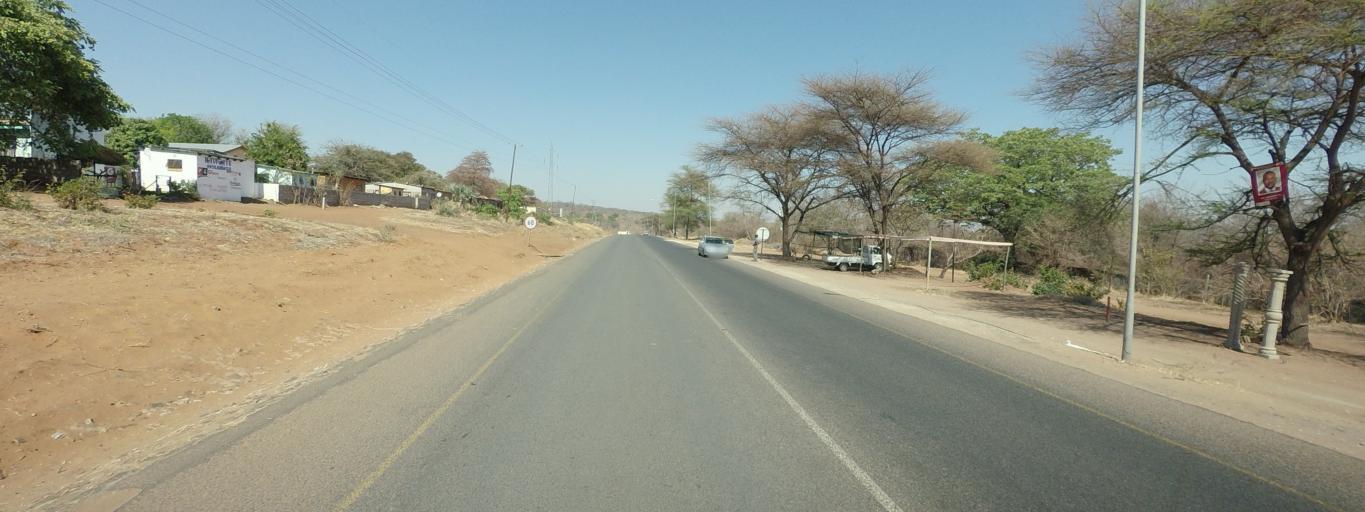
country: BW
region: North West
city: Kasane
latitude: -17.7993
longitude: 25.2277
